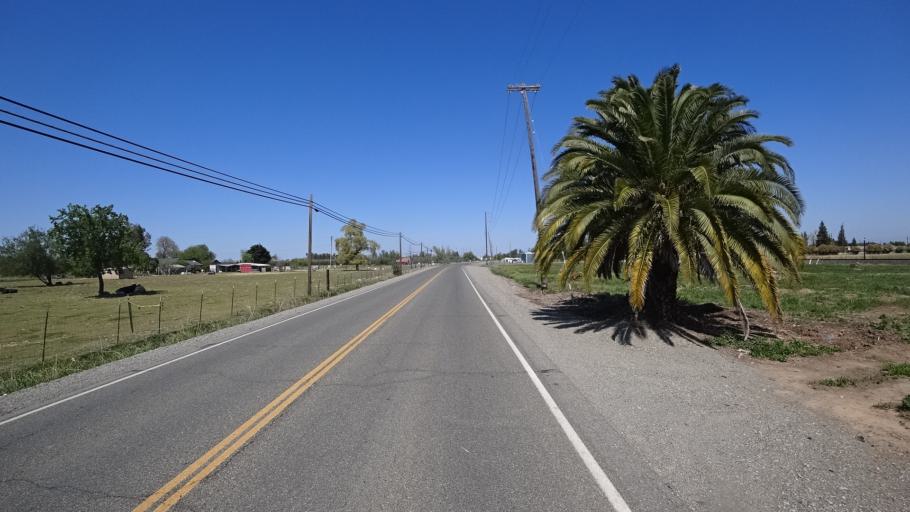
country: US
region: California
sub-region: Glenn County
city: Orland
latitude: 39.7244
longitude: -122.1969
